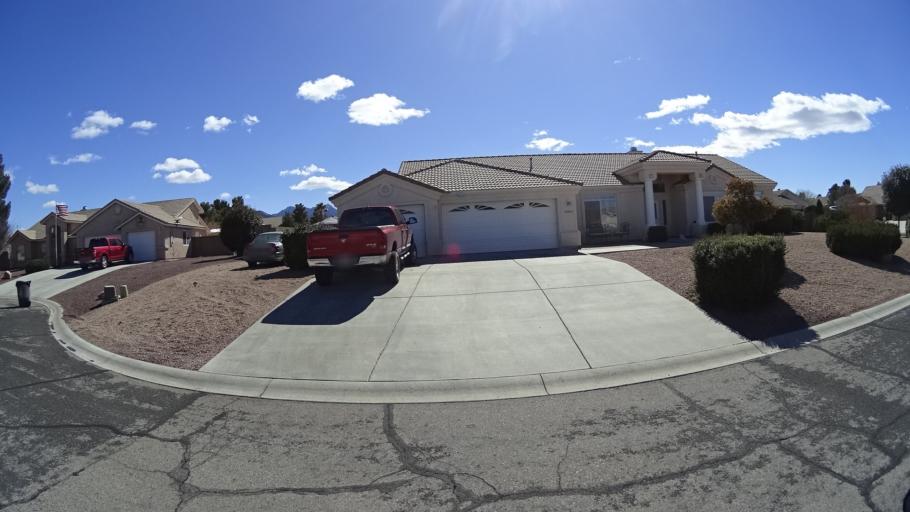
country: US
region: Arizona
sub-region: Mohave County
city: Kingman
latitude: 35.2065
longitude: -113.9728
